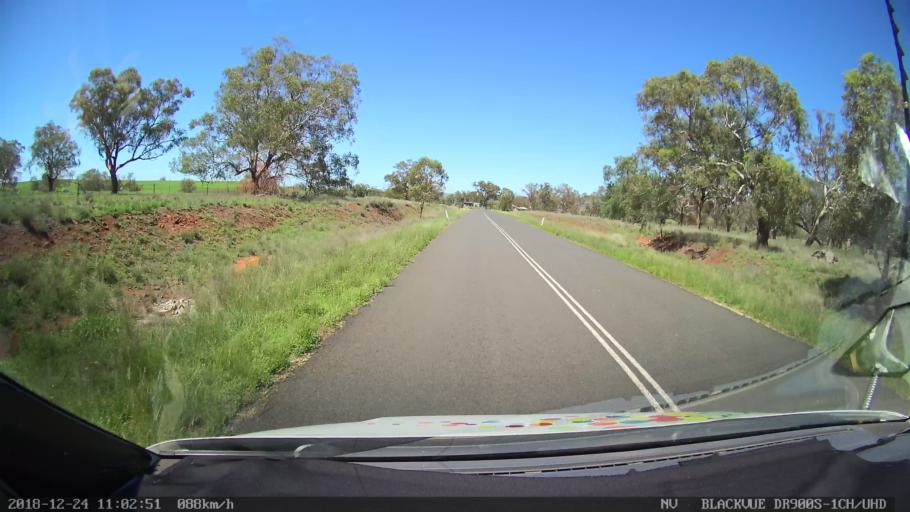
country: AU
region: New South Wales
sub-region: Upper Hunter Shire
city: Merriwa
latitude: -32.0895
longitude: 150.3716
